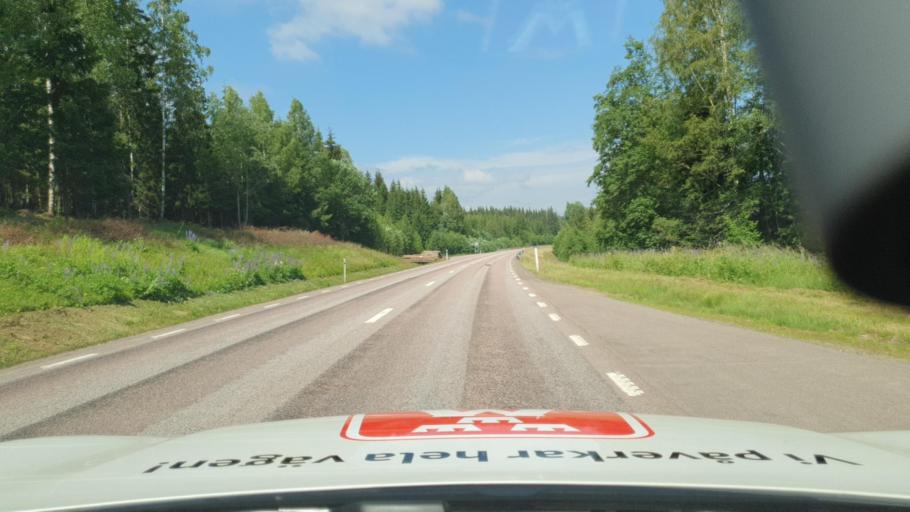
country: SE
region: Vaermland
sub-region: Torsby Kommun
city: Torsby
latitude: 60.0759
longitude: 13.0374
